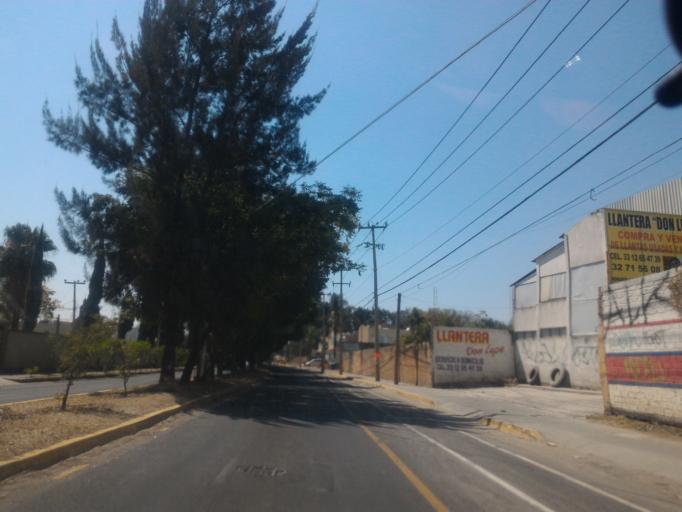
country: MX
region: Jalisco
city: Santa Anita
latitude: 20.5544
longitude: -103.4549
